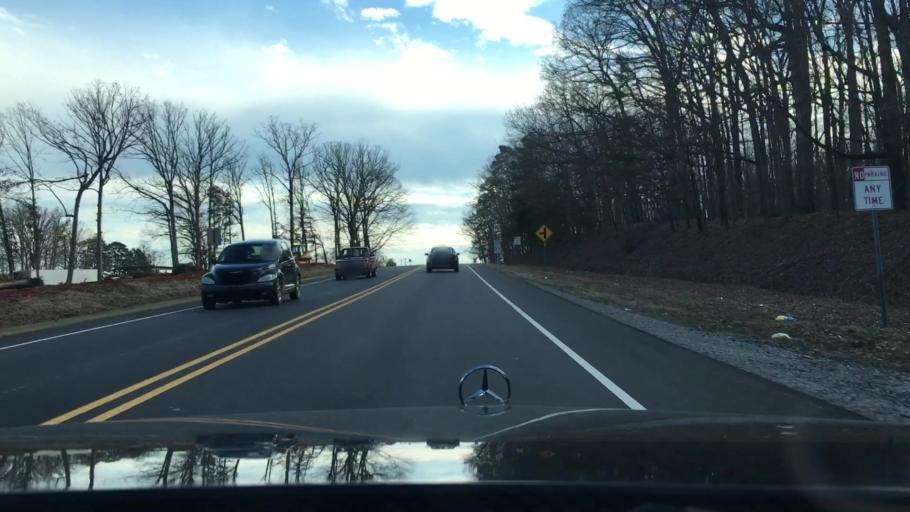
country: US
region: Virginia
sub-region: City of Danville
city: Danville
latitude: 36.5393
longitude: -79.4006
